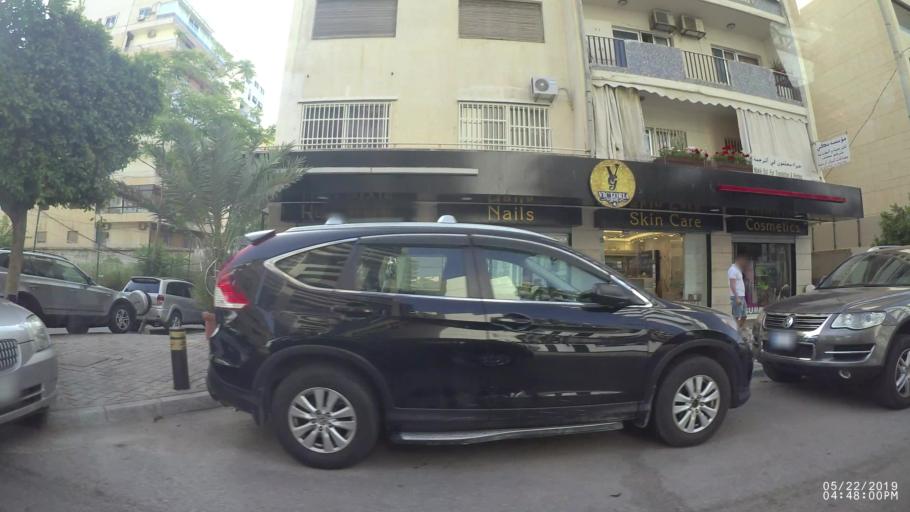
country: LB
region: Beyrouth
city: Ra's Bayrut
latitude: 33.8950
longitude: 35.4736
